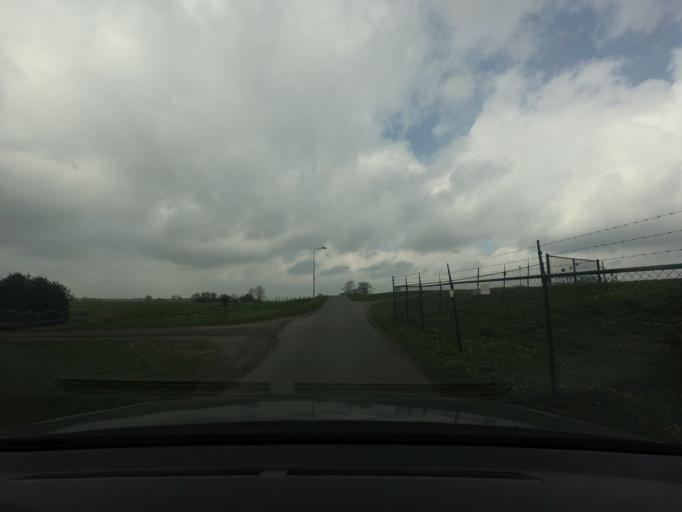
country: NL
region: Utrecht
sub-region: Gemeente De Ronde Venen
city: Mijdrecht
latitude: 52.1877
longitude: 4.8253
